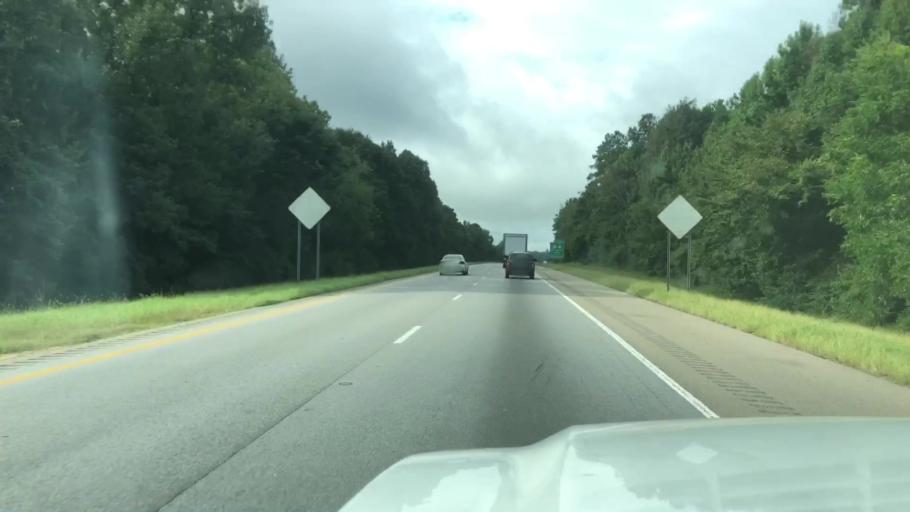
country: US
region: Alabama
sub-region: Lowndes County
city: Fort Deposit
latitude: 31.9994
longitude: -86.5249
